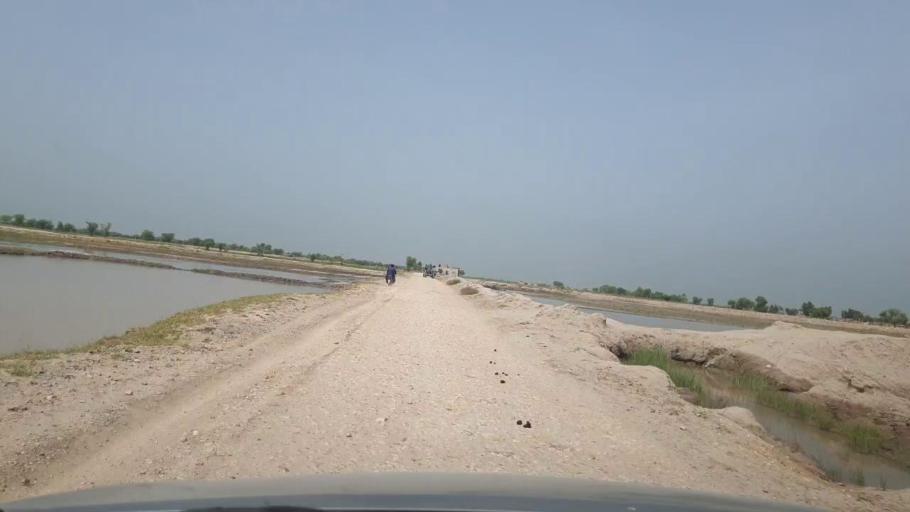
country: PK
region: Sindh
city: Garhi Yasin
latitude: 27.9119
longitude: 68.4075
